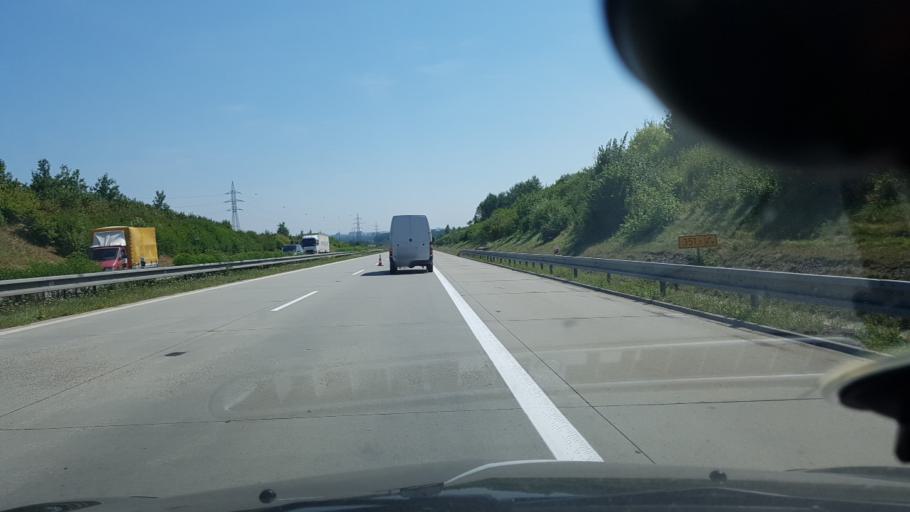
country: CZ
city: Klimkovice
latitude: 49.8006
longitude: 18.1671
